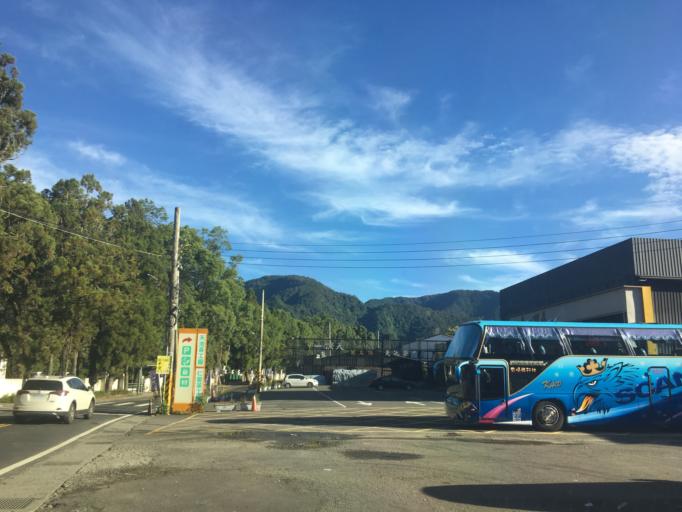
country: TW
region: Taiwan
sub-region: Nantou
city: Puli
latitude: 24.0318
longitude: 121.1426
